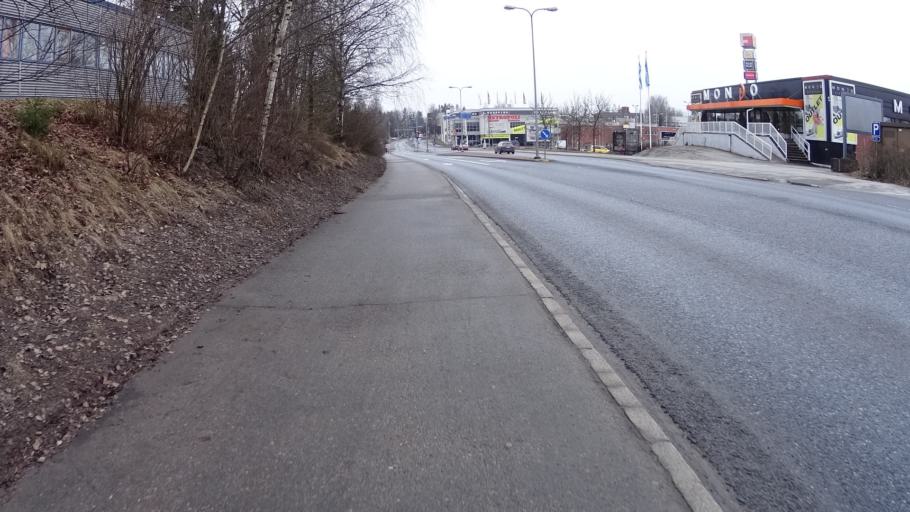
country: FI
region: Uusimaa
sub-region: Helsinki
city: Kilo
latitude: 60.2775
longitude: 24.8211
